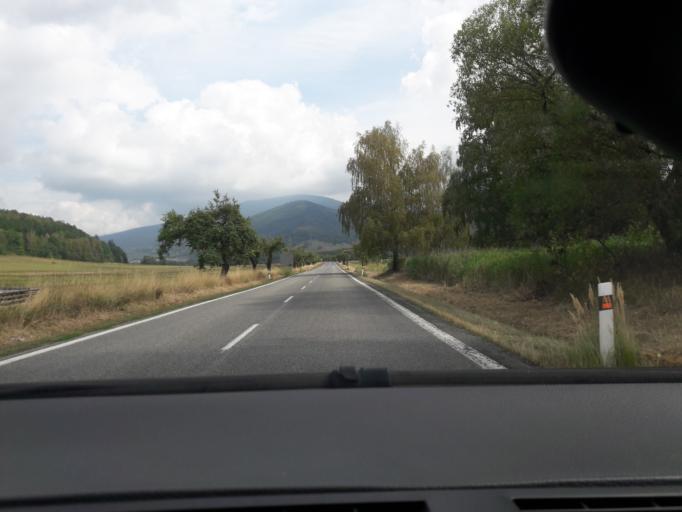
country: CZ
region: Olomoucky
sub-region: Okres Sumperk
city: Velke Losiny
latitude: 50.0426
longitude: 17.0606
